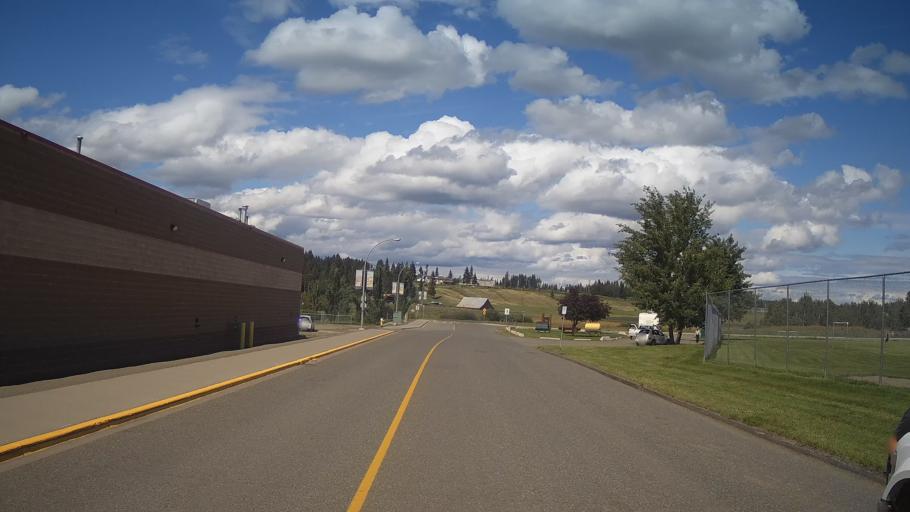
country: CA
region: British Columbia
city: Cache Creek
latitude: 51.6477
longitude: -121.2943
